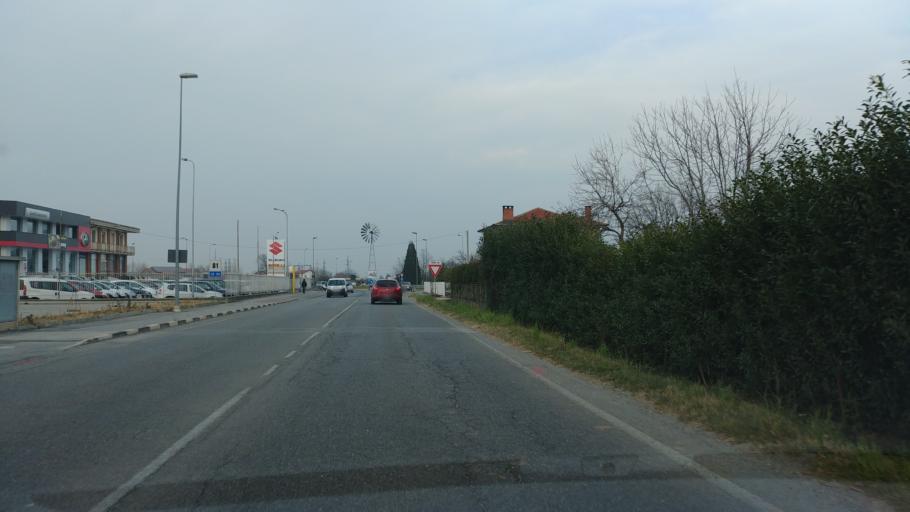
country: IT
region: Piedmont
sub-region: Provincia di Cuneo
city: Borgo San Dalmazzo
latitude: 44.3524
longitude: 7.5097
